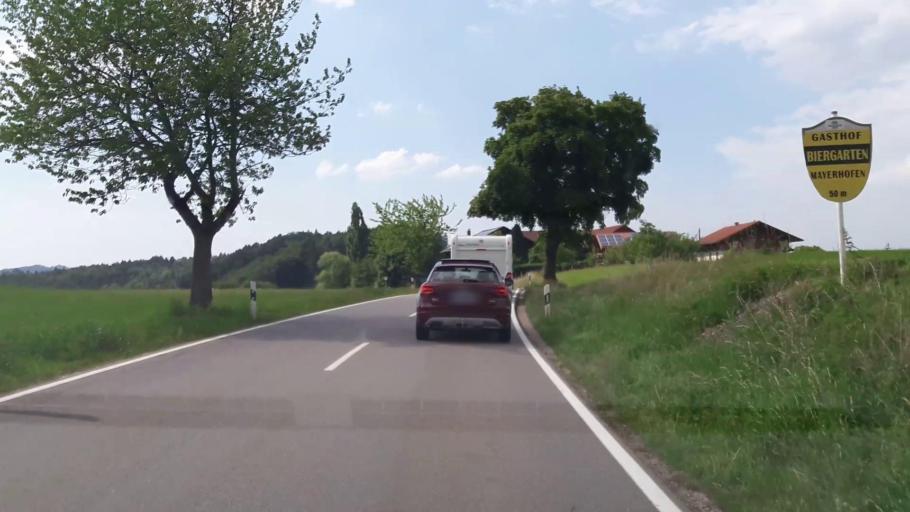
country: DE
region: Bavaria
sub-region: Upper Bavaria
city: Anger
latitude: 47.8190
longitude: 12.8501
